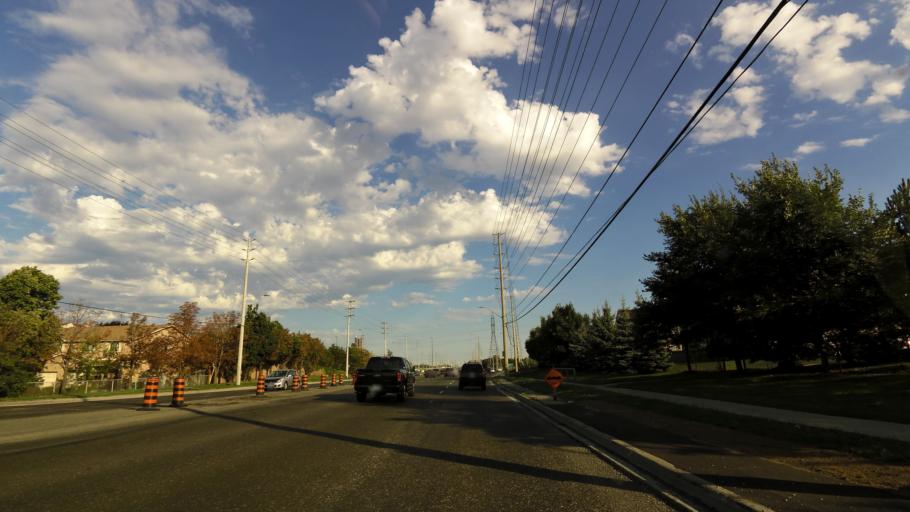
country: CA
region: Ontario
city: Mississauga
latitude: 43.5890
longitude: -79.6650
